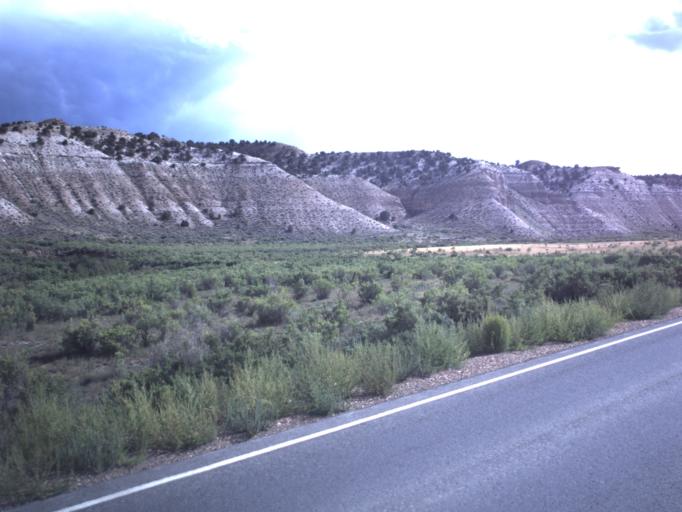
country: US
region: Utah
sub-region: Duchesne County
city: Duchesne
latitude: 40.1304
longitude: -110.4339
